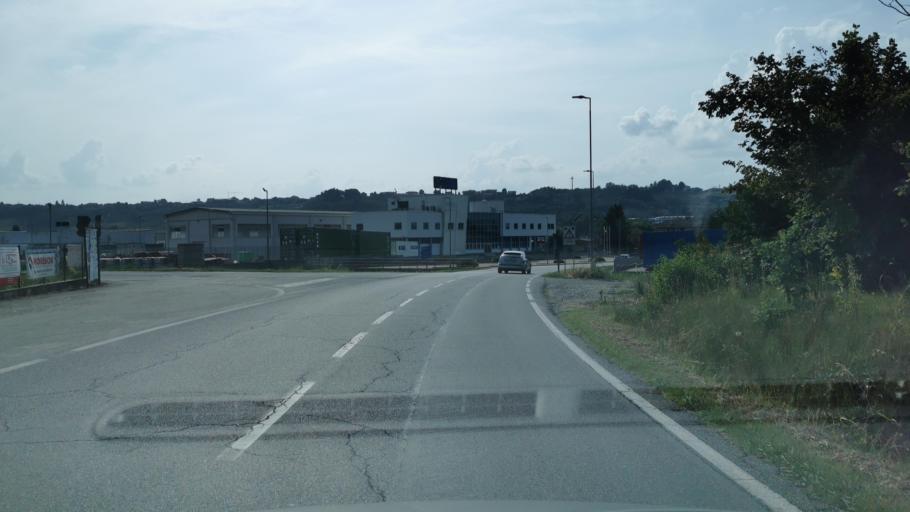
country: IT
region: Piedmont
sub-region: Provincia di Cuneo
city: Cherasco
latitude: 44.6458
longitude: 7.8784
